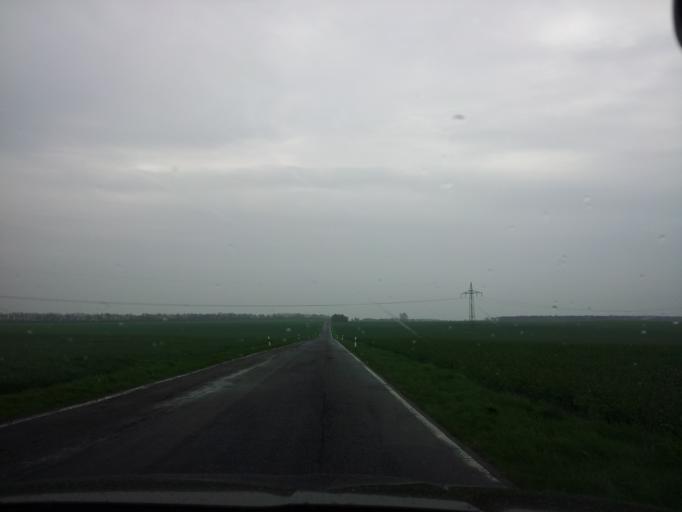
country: DE
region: Saxony-Anhalt
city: Kropstadt
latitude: 51.9832
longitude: 12.8094
